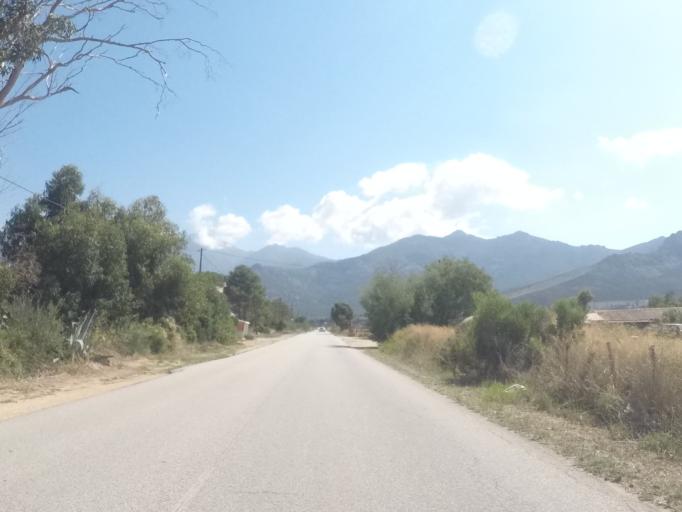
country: FR
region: Corsica
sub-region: Departement de la Haute-Corse
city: Calenzana
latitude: 42.5001
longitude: 8.7929
